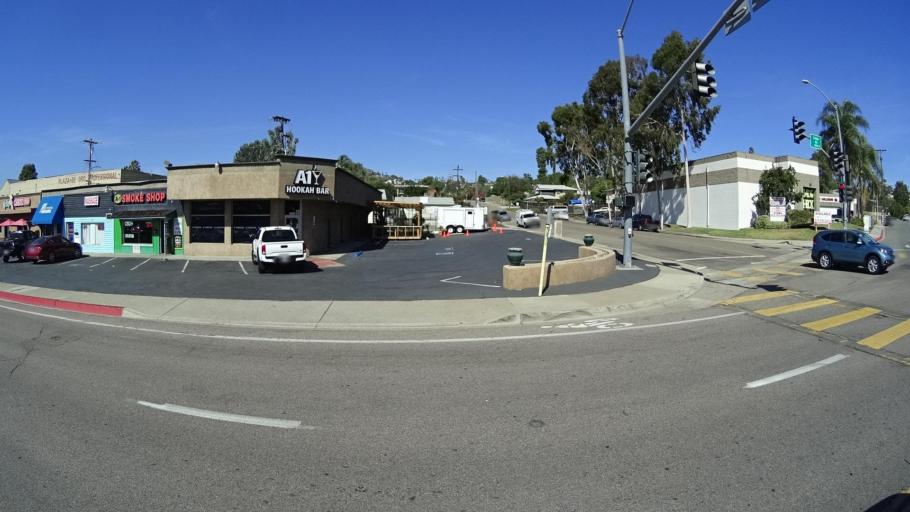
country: US
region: California
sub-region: San Diego County
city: Casa de Oro-Mount Helix
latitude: 32.7479
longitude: -116.9792
